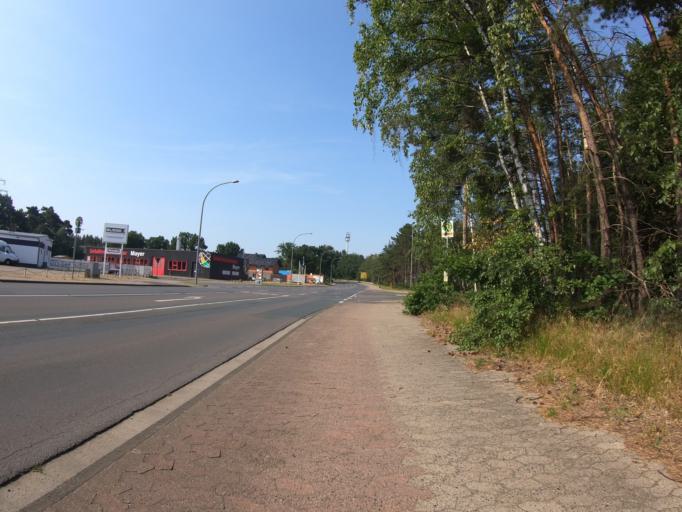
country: DE
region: Lower Saxony
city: Gifhorn
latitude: 52.4719
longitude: 10.5326
